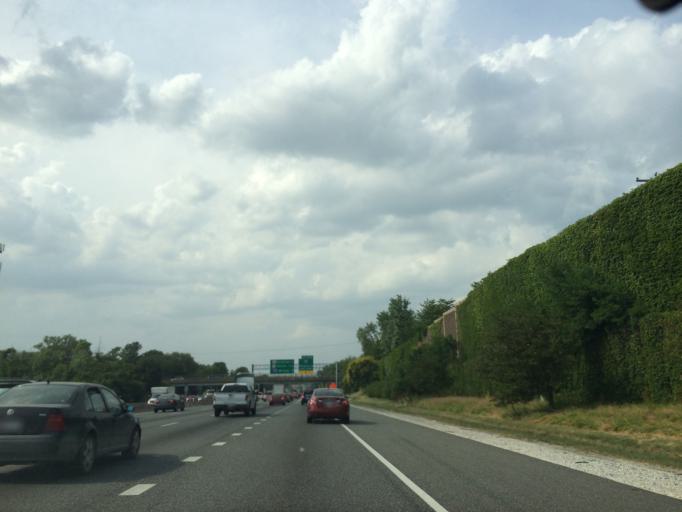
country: US
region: Maryland
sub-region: Baltimore County
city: Catonsville
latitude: 39.2951
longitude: -76.7424
